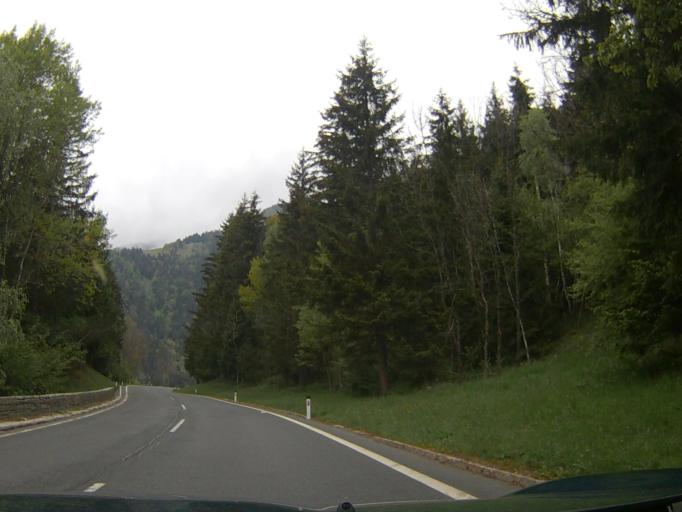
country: AT
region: Carinthia
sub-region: Politischer Bezirk Spittal an der Drau
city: Obervellach
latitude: 46.9433
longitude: 13.1876
